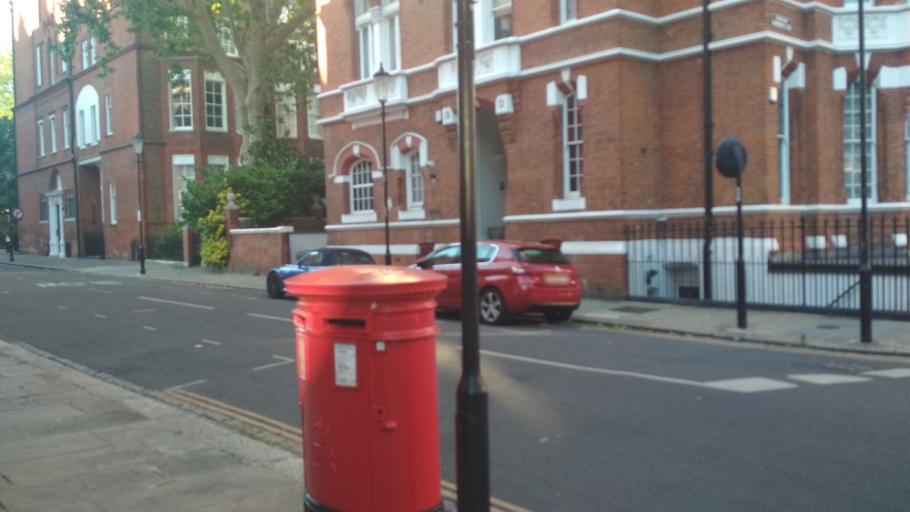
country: GB
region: England
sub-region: Greater London
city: Chelsea
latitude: 51.4937
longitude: -0.1608
